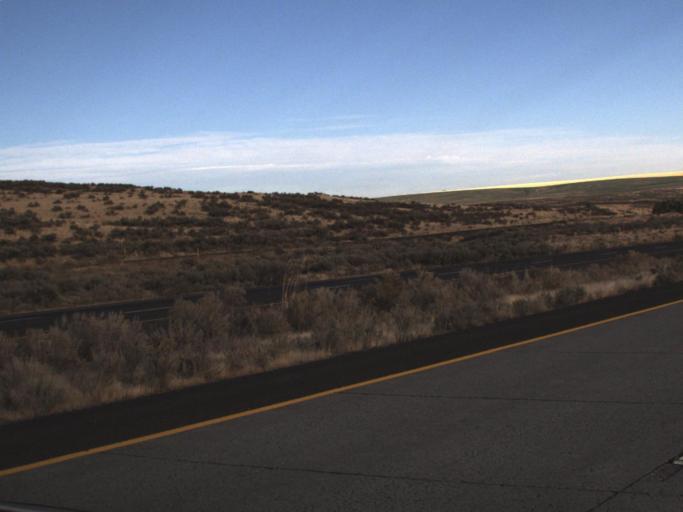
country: US
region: Washington
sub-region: Adams County
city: Ritzville
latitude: 46.9564
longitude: -118.5745
